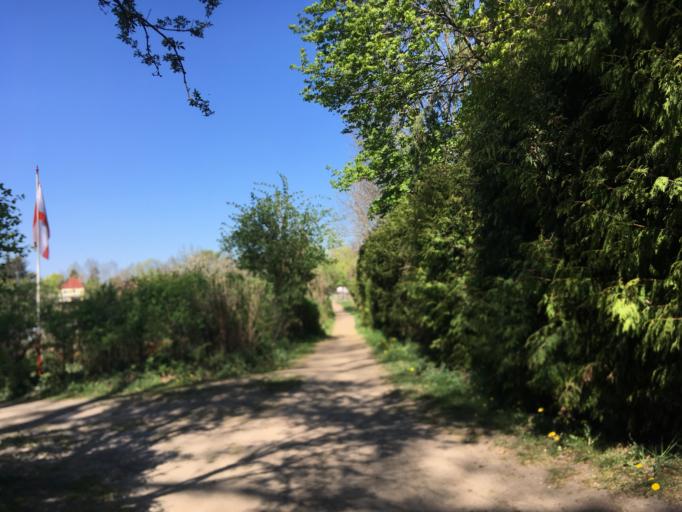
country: DE
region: Berlin
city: Buch
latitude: 52.6414
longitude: 13.5071
